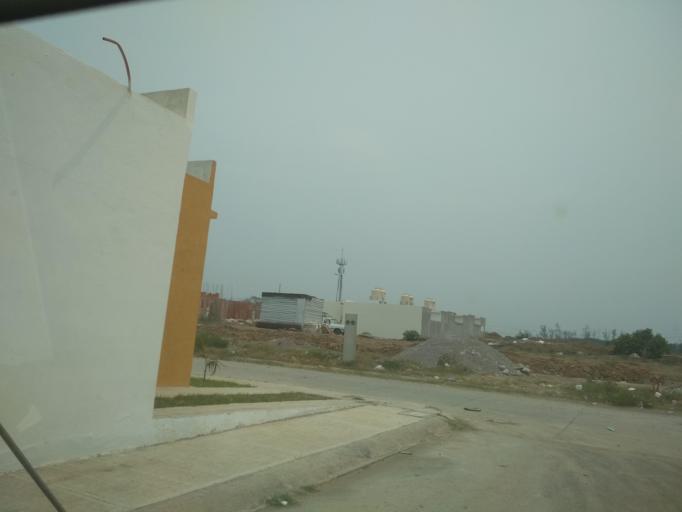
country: MX
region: Veracruz
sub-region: Veracruz
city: Las Amapolas
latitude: 19.1527
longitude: -96.2185
